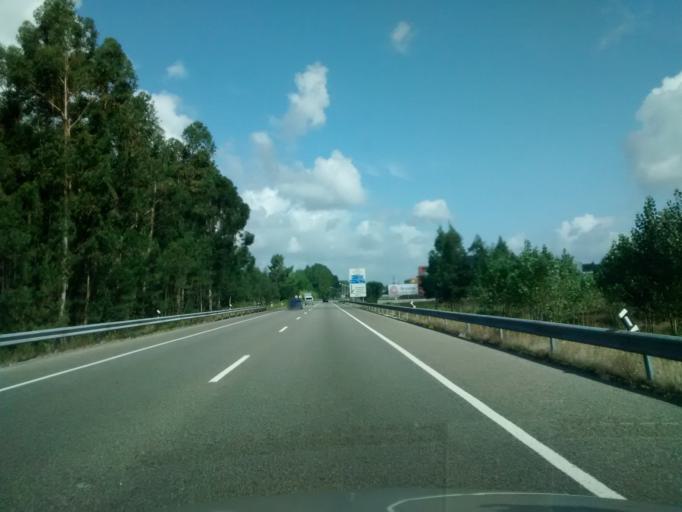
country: PT
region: Aveiro
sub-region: Anadia
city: Sangalhos
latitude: 40.4762
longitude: -8.4743
